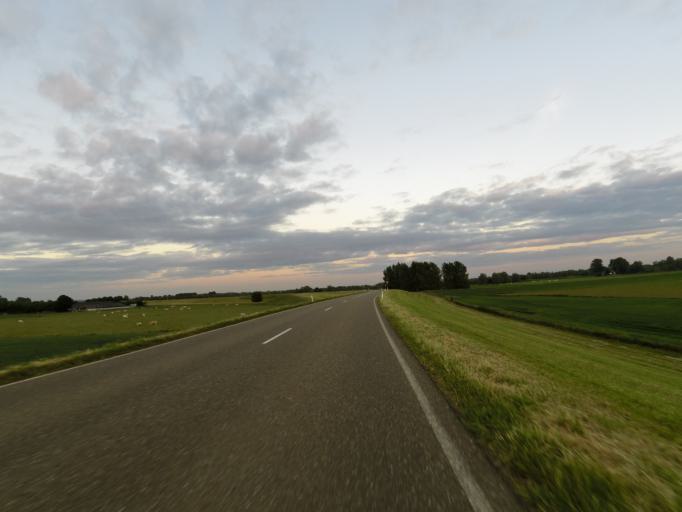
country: NL
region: Gelderland
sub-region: Gemeente Zevenaar
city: Zevenaar
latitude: 51.8834
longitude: 6.0639
